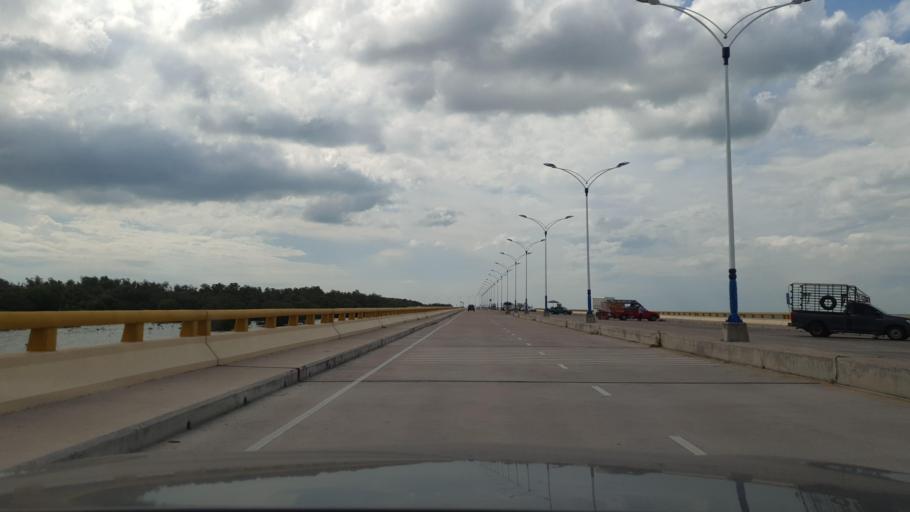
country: TH
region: Chon Buri
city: Chon Buri
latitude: 13.3498
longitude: 100.9544
